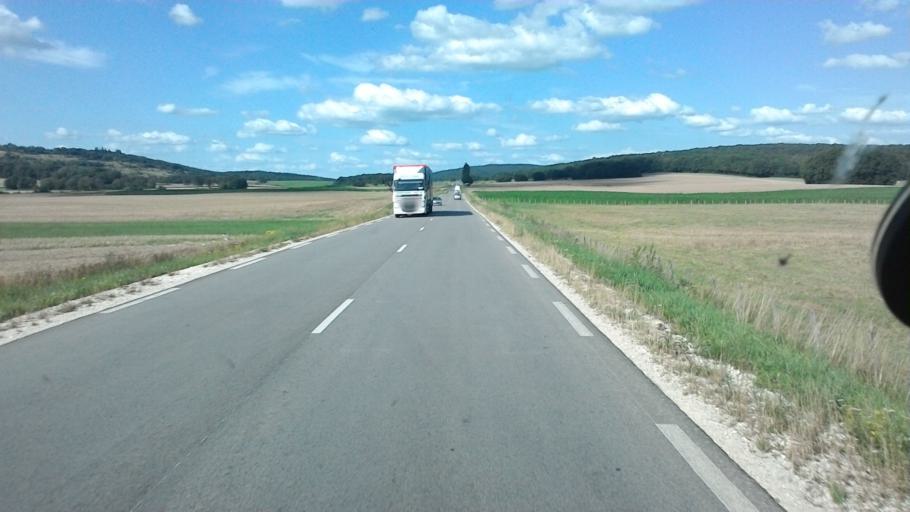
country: FR
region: Franche-Comte
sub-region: Departement de la Haute-Saone
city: Noidans-les-Vesoul
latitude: 47.5621
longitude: 6.0728
